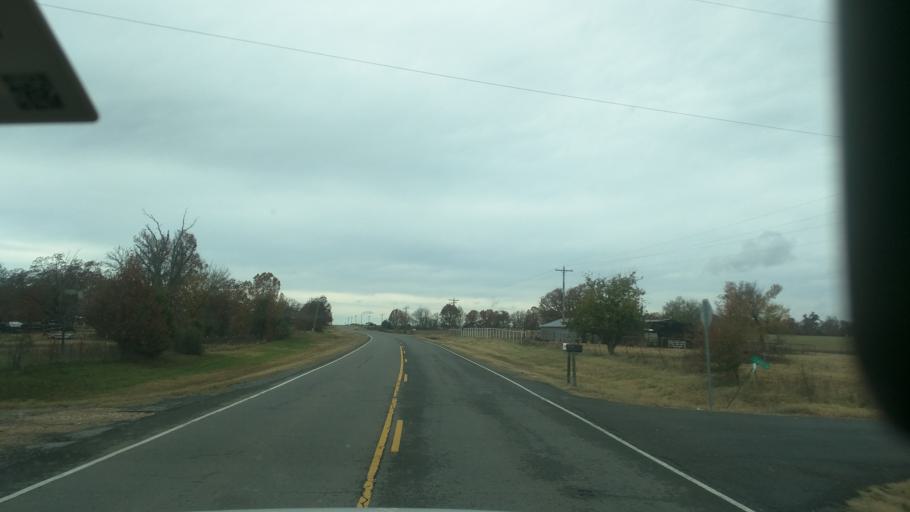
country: US
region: Oklahoma
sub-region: Adair County
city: Stilwell
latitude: 35.8953
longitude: -94.7810
